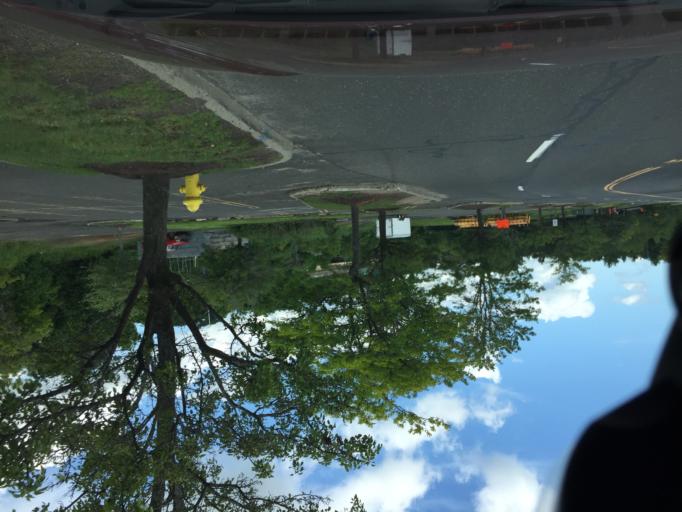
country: US
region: Connecticut
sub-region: Fairfield County
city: Danbury
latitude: 41.3808
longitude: -73.4761
